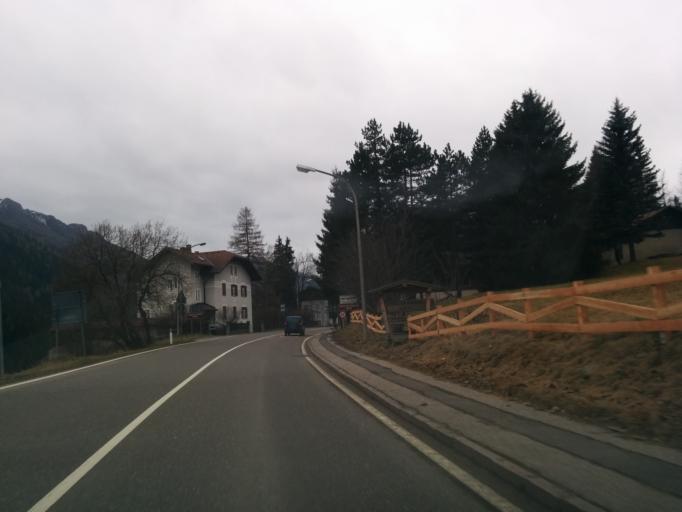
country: IT
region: Trentino-Alto Adige
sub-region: Provincia di Trento
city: Pozza di Fassa
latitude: 46.4221
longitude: 11.6824
